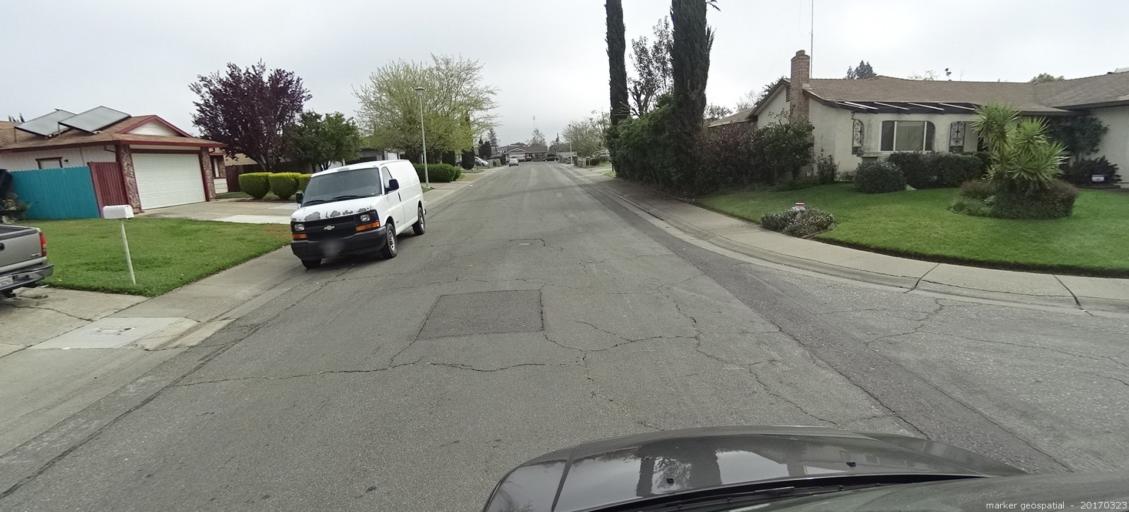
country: US
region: California
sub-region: Sacramento County
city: Florin
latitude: 38.5130
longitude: -121.4180
